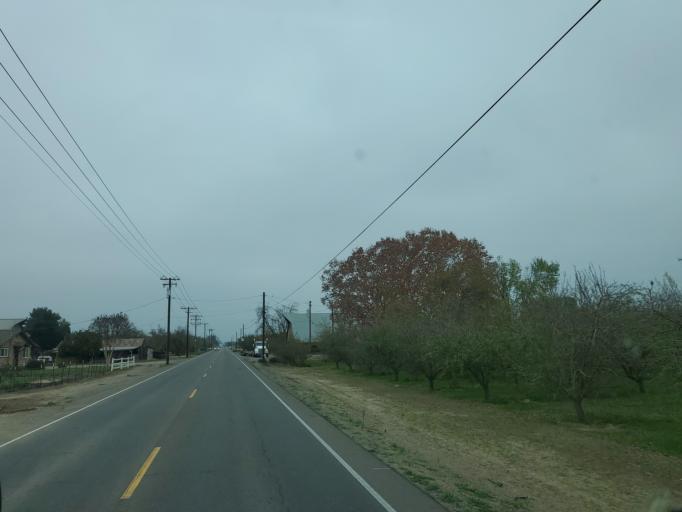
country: US
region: California
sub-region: Stanislaus County
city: Keyes
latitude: 37.5512
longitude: -120.8738
